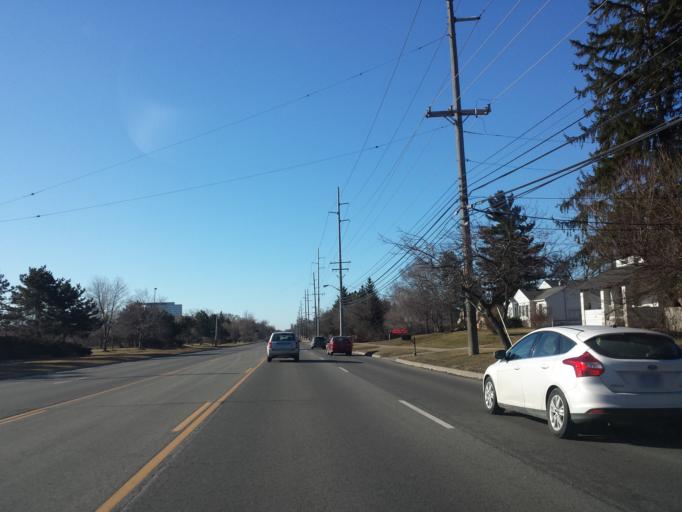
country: US
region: Michigan
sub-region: Oakland County
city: Troy
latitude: 42.5722
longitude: -83.1482
